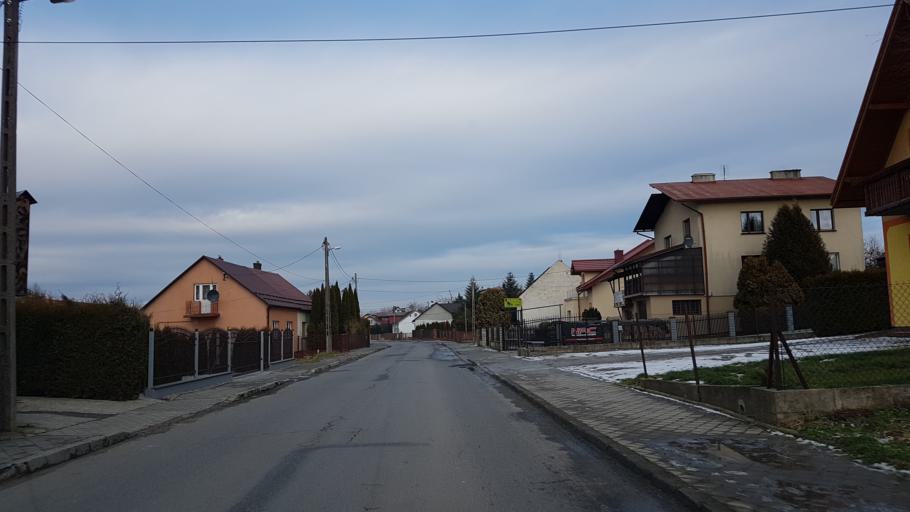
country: PL
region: Lesser Poland Voivodeship
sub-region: Powiat nowosadecki
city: Stary Sacz
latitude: 49.5493
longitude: 20.6289
